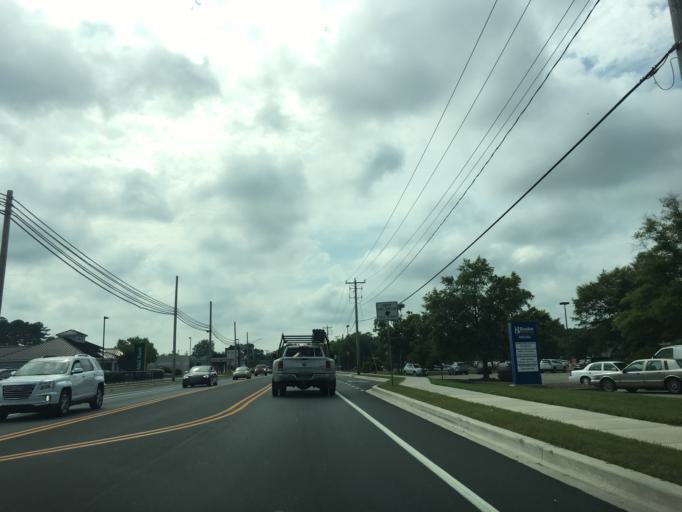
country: US
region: Delaware
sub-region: Sussex County
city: Ocean View
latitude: 38.5469
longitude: -75.1061
